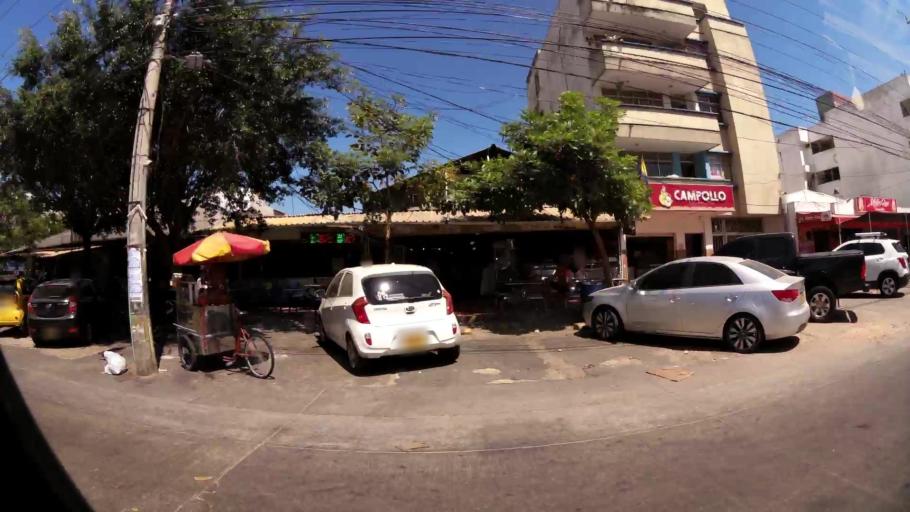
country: CO
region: Atlantico
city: Barranquilla
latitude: 10.9928
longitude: -74.8091
